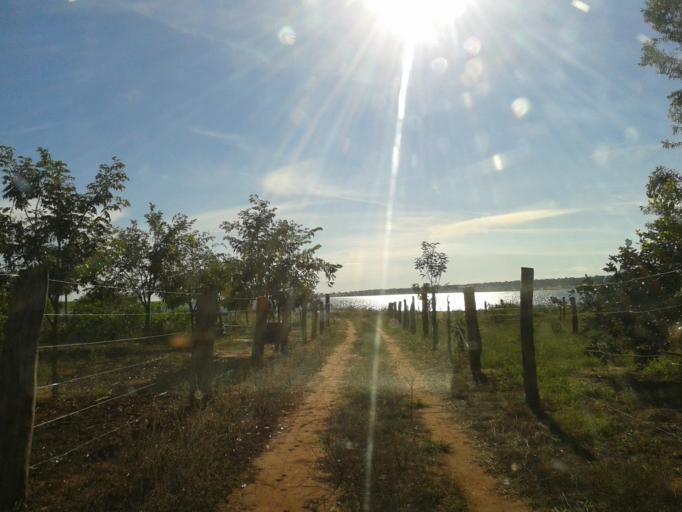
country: BR
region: Minas Gerais
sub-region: Santa Vitoria
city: Santa Vitoria
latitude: -19.0008
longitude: -50.3873
